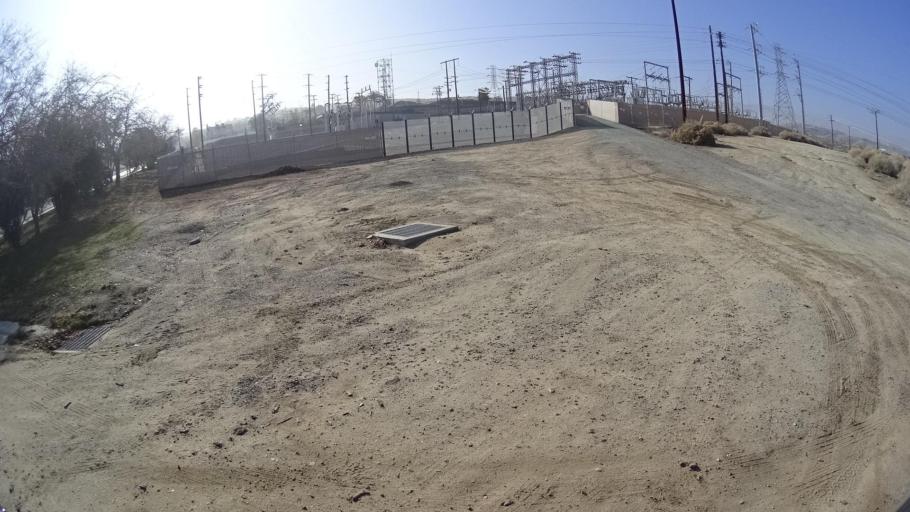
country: US
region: California
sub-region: Kern County
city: Taft Heights
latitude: 35.1370
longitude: -119.4812
